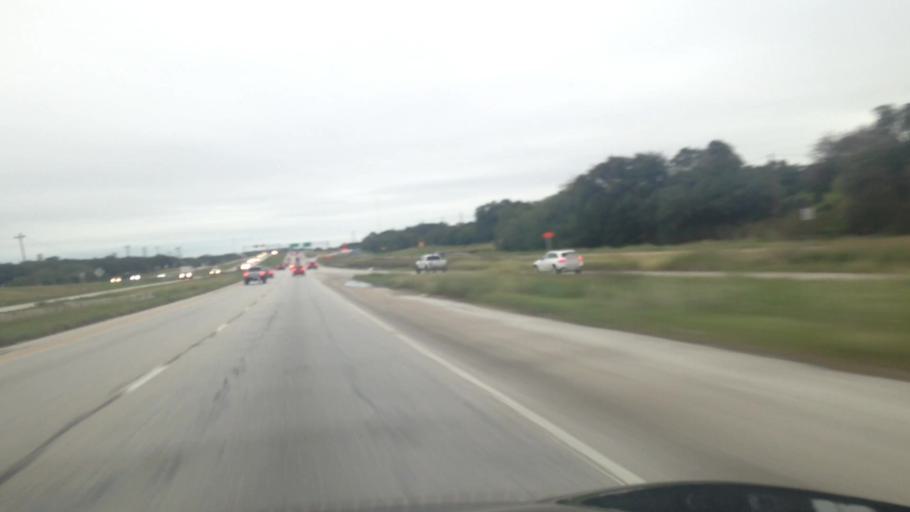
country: US
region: Texas
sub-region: Bexar County
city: Hollywood Park
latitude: 29.6009
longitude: -98.4151
